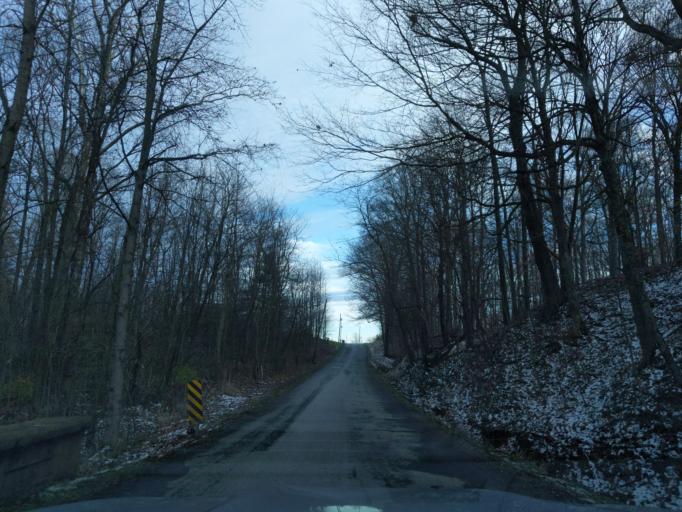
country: US
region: Indiana
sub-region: Decatur County
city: Westport
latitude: 39.2194
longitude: -85.5012
